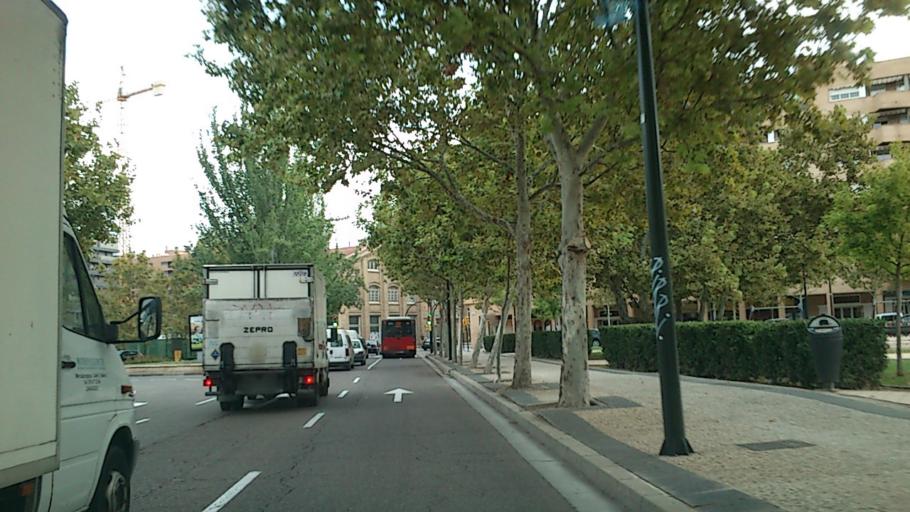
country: ES
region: Aragon
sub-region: Provincia de Zaragoza
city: Zaragoza
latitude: 41.6605
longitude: -0.8675
